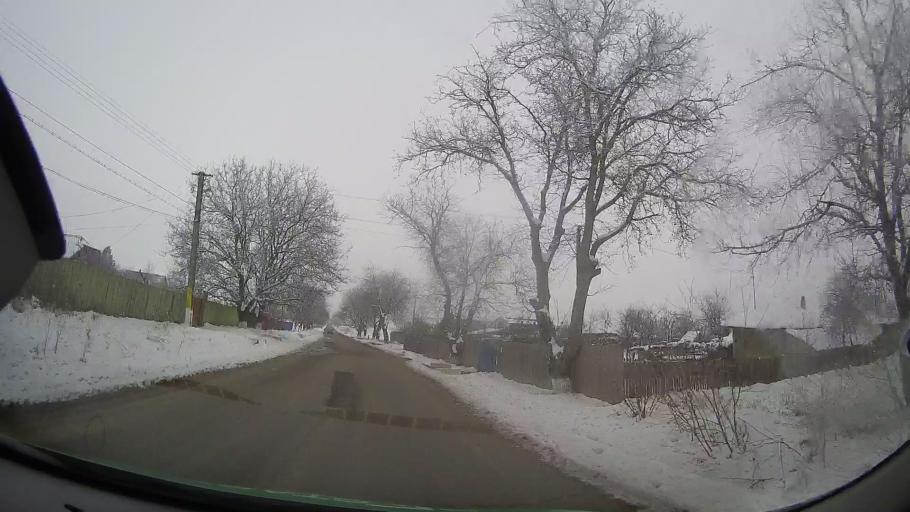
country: RO
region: Bacau
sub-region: Comuna Oncesti
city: Oncesti
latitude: 46.4509
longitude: 27.2621
